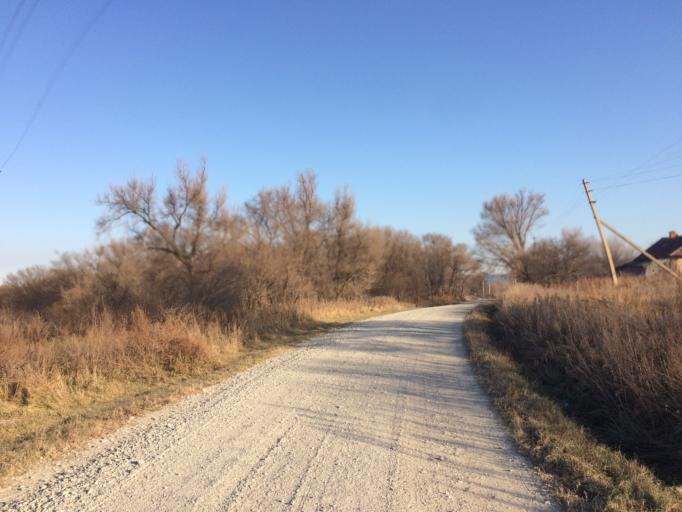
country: RU
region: Primorskiy
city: Ivanovka
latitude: 43.9573
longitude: 132.4782
